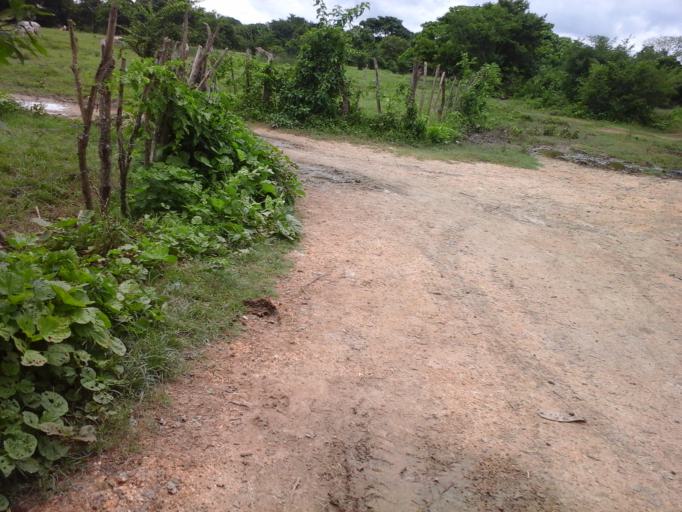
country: CO
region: Bolivar
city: San Pablo
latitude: 10.1520
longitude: -75.2732
